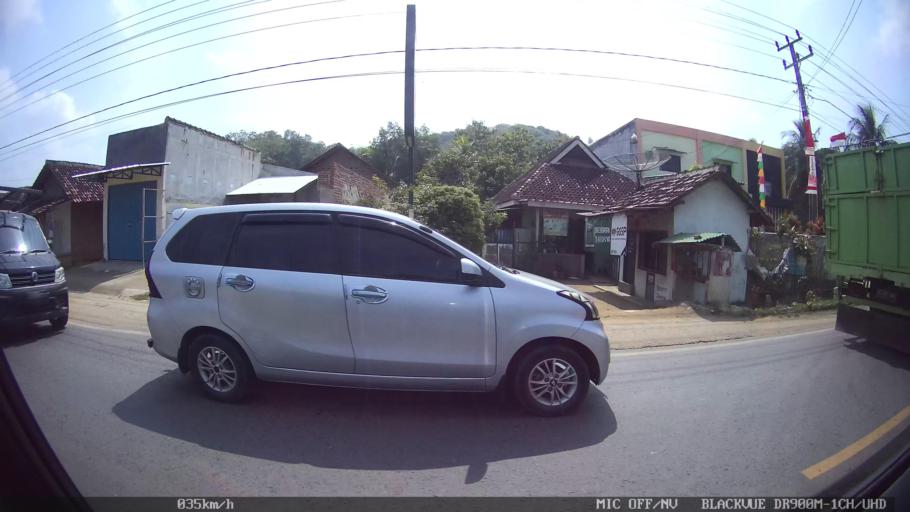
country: ID
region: Lampung
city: Pringsewu
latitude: -5.3776
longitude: 105.0148
